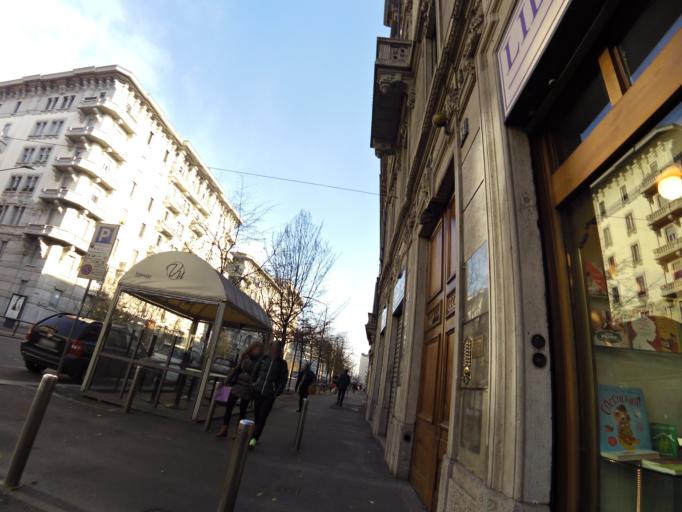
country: IT
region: Lombardy
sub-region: Citta metropolitana di Milano
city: Milano
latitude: 45.4621
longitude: 9.1989
